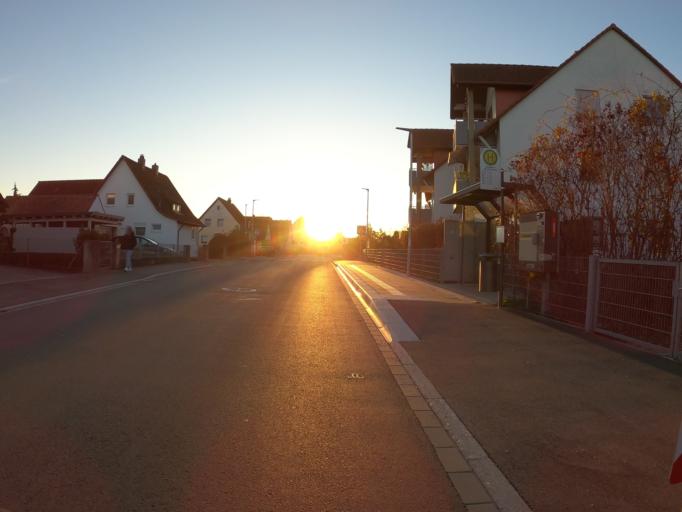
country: DE
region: Bavaria
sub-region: Swabia
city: Holzheim
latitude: 48.4164
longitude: 10.0652
